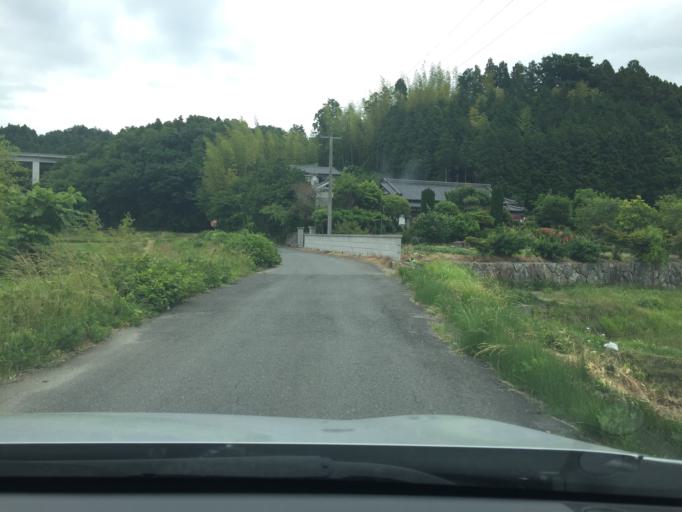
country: JP
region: Fukushima
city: Iwaki
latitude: 37.1141
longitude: 140.9069
